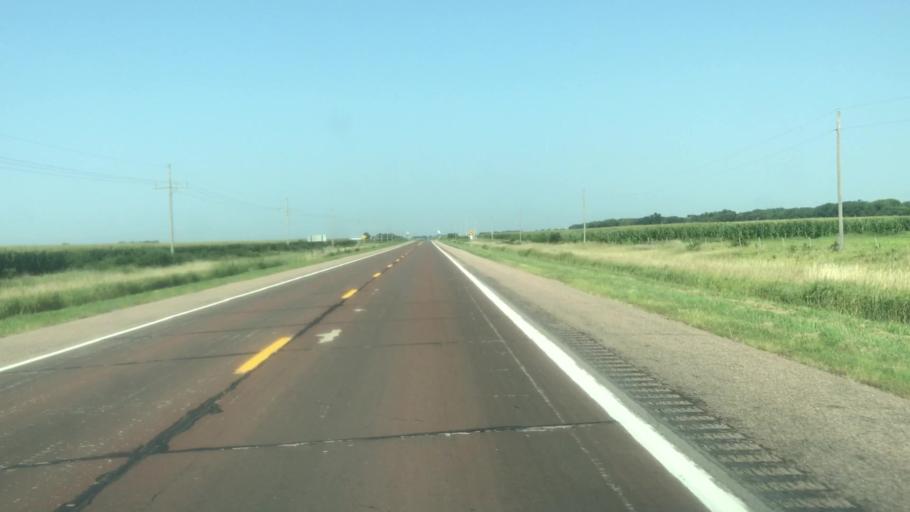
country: US
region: Nebraska
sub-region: Hall County
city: Grand Island
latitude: 40.9674
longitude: -98.4570
